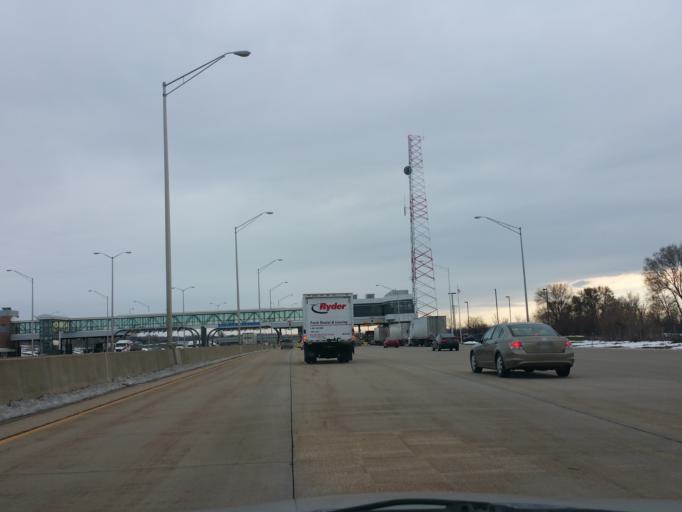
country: US
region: Illinois
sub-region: Winnebago County
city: Roscoe
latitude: 42.4470
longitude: -88.9934
